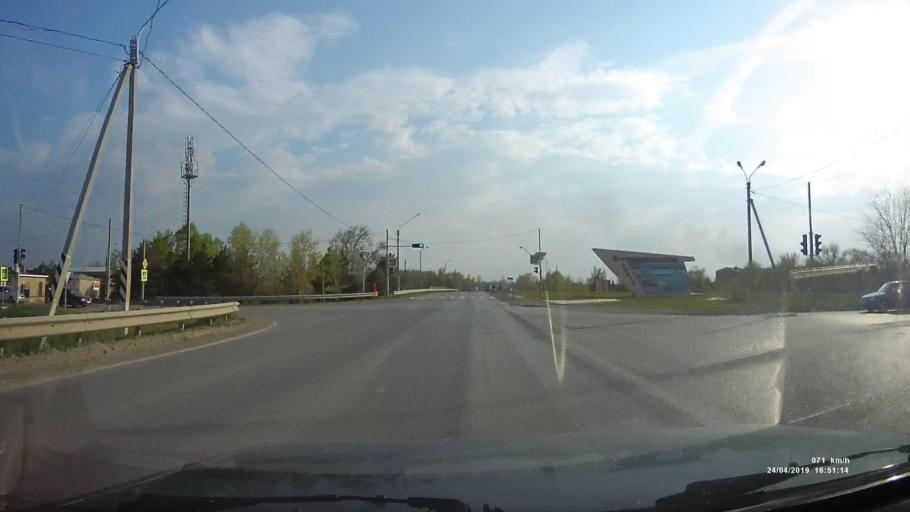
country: RU
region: Rostov
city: Proletarsk
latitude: 46.6983
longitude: 41.7485
